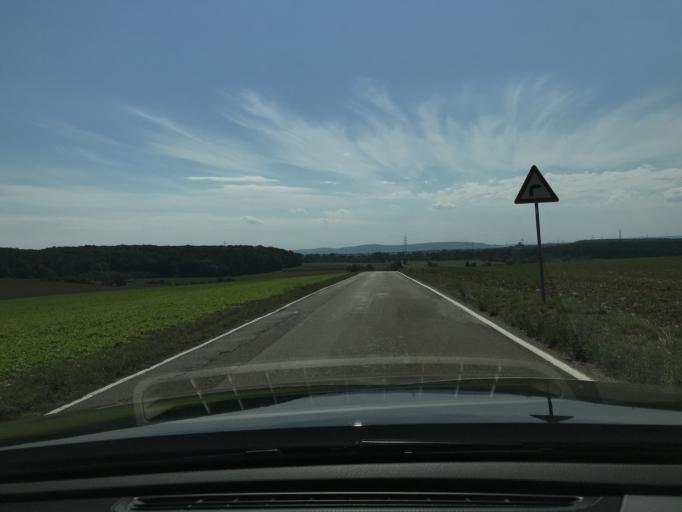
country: DE
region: Baden-Wuerttemberg
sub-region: Regierungsbezirk Stuttgart
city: Affalterbach
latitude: 48.9121
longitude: 9.3150
